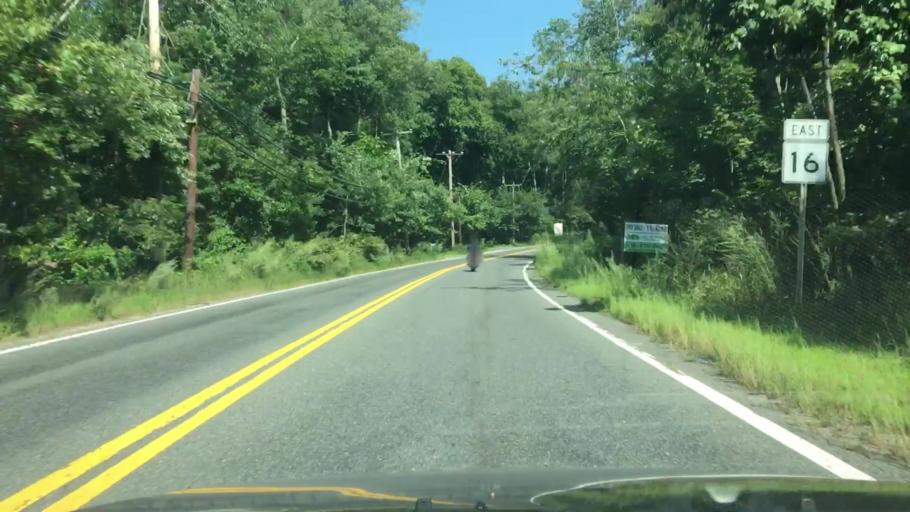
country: US
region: Massachusetts
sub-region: Middlesex County
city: Holliston
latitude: 42.1786
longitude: -71.4575
